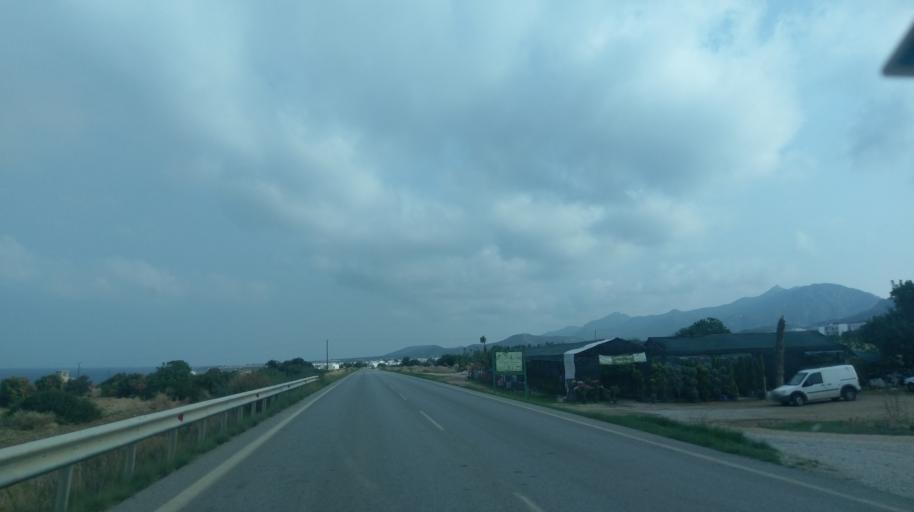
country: CY
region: Ammochostos
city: Lefkonoiko
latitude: 35.3609
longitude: 33.6675
